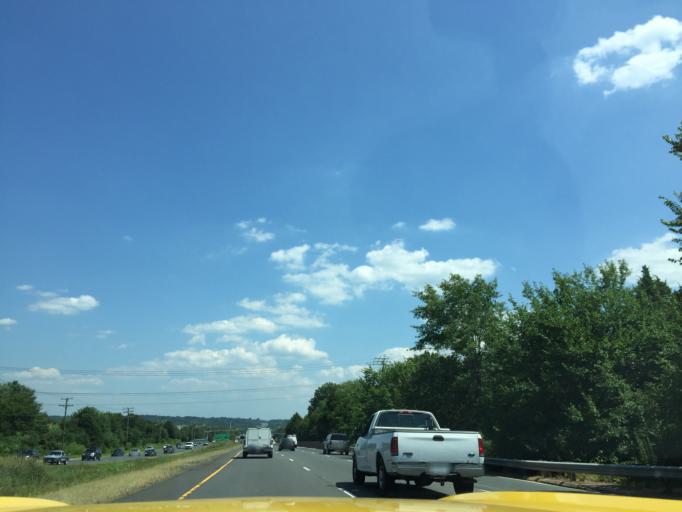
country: US
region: Virginia
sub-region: Loudoun County
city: Sugarland Run
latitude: 39.0236
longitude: -77.3888
